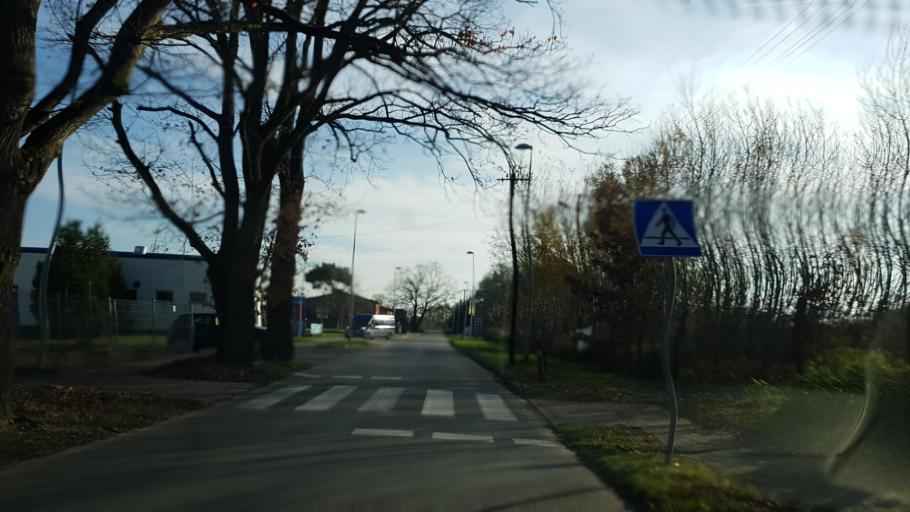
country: PL
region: West Pomeranian Voivodeship
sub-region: Powiat policki
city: Dobra
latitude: 53.4885
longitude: 14.3791
